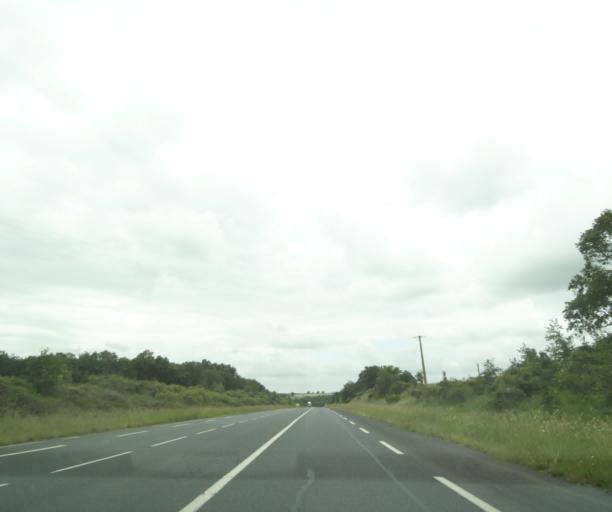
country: FR
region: Poitou-Charentes
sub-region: Departement des Deux-Sevres
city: Saint-Varent
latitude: 46.9087
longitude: -0.1927
